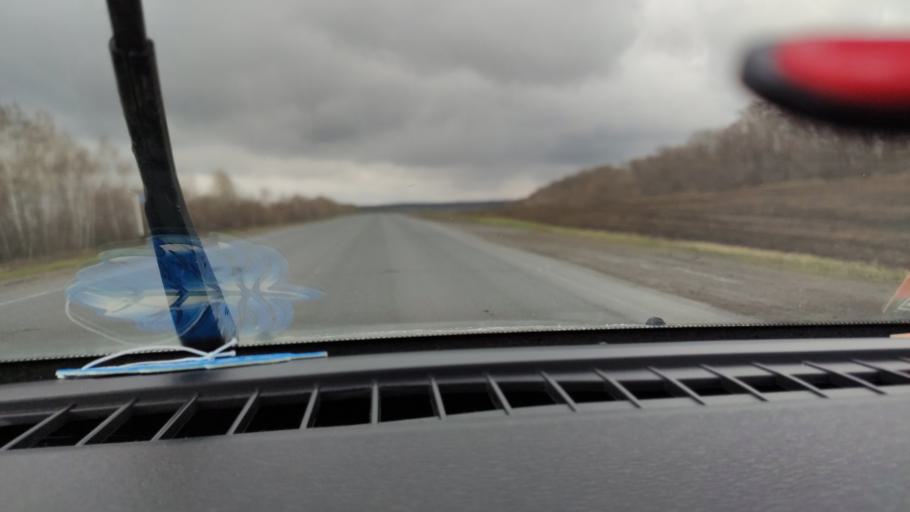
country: RU
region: Samara
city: Koshki
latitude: 54.1673
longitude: 50.4210
